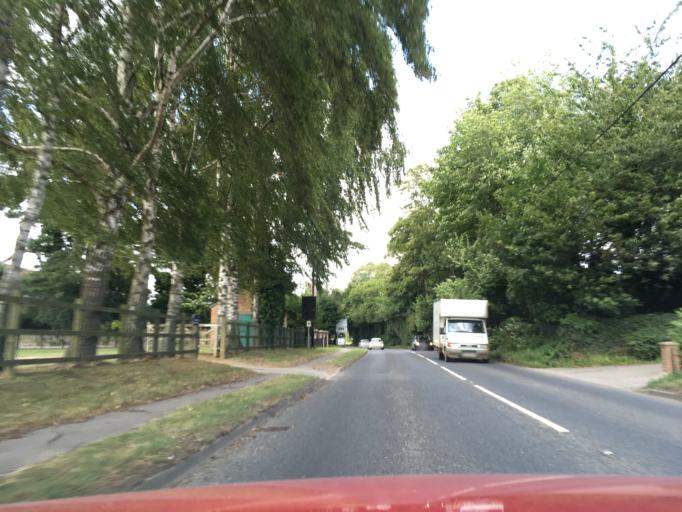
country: GB
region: England
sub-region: Kent
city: Headcorn
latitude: 51.2198
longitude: 0.5933
